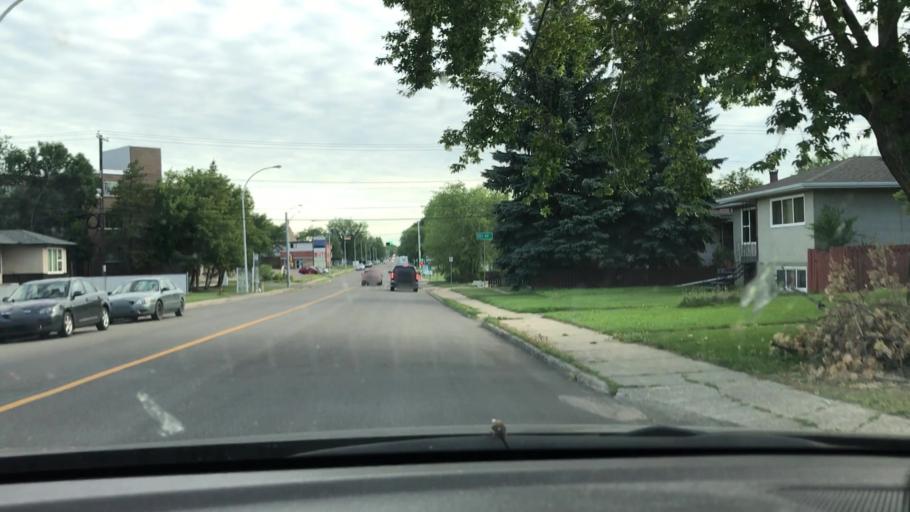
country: CA
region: Alberta
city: Edmonton
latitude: 53.5401
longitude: -113.4493
